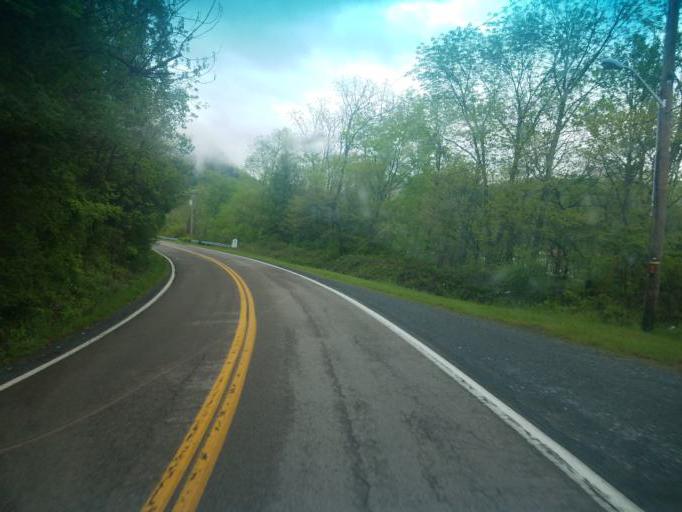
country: US
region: Virginia
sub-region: Washington County
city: Emory
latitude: 36.6376
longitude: -81.7909
